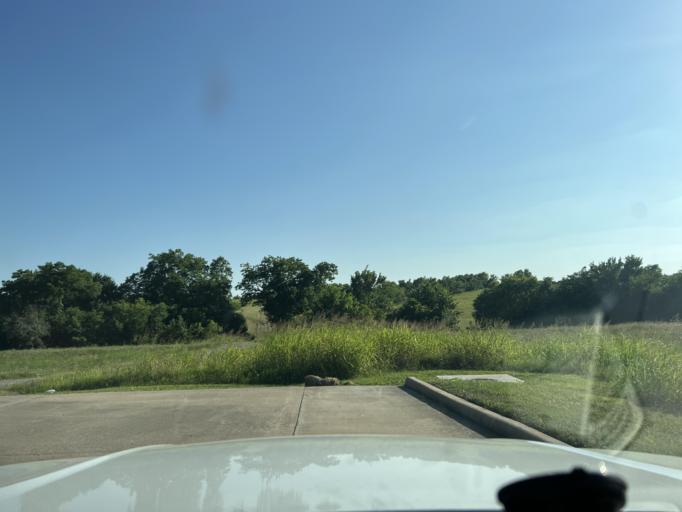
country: US
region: Texas
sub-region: Washington County
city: Brenham
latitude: 30.1374
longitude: -96.3696
